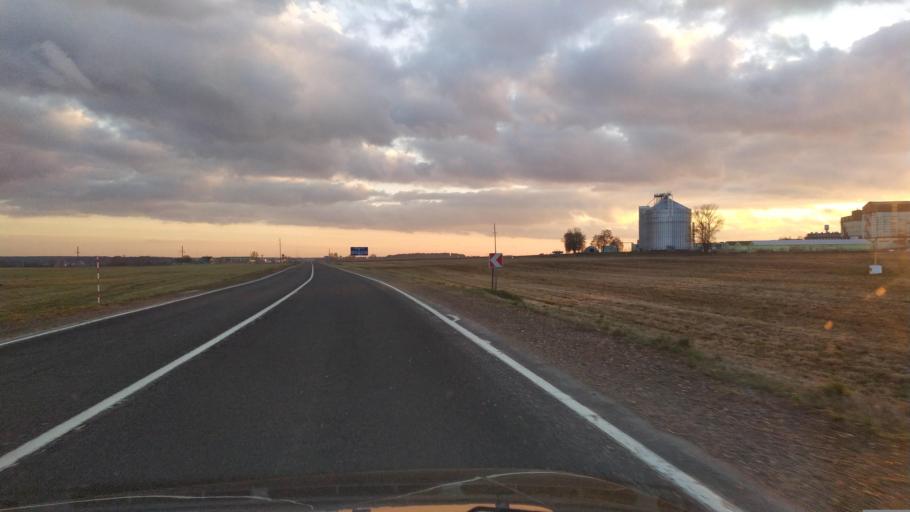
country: BY
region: Brest
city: Kamyanyets
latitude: 52.4040
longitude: 23.7840
